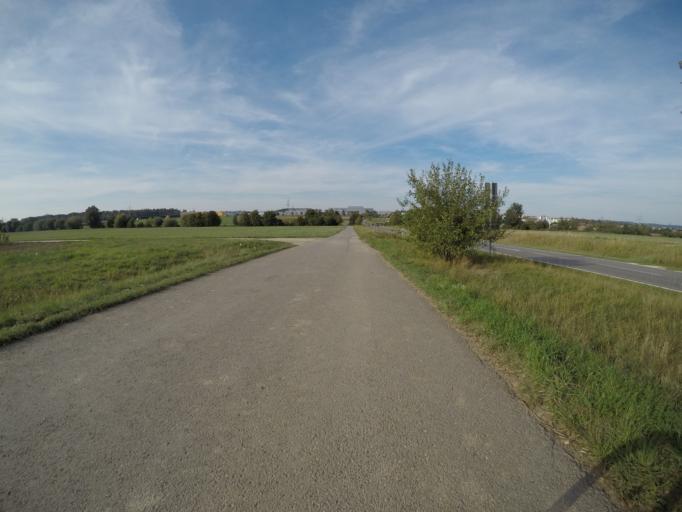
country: DE
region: Baden-Wuerttemberg
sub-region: Regierungsbezirk Stuttgart
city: Ostfildern
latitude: 48.6999
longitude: 9.2475
